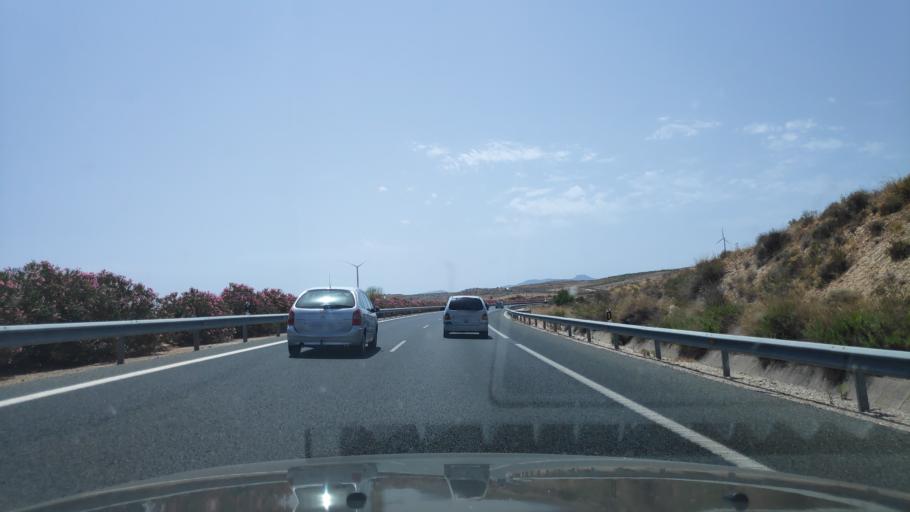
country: ES
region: Andalusia
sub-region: Provincia de Granada
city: Padul
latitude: 37.0185
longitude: -3.6409
